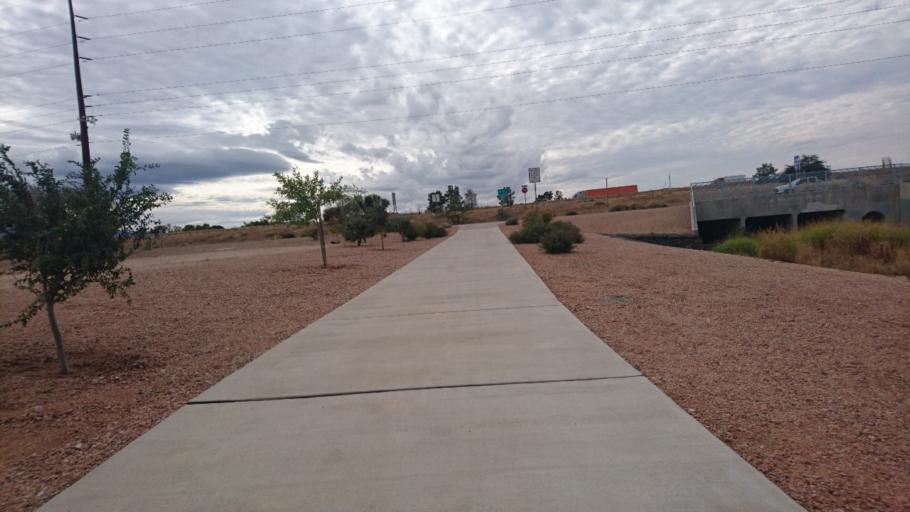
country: US
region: Arizona
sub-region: Mohave County
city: Kingman
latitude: 35.2190
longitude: -114.0316
